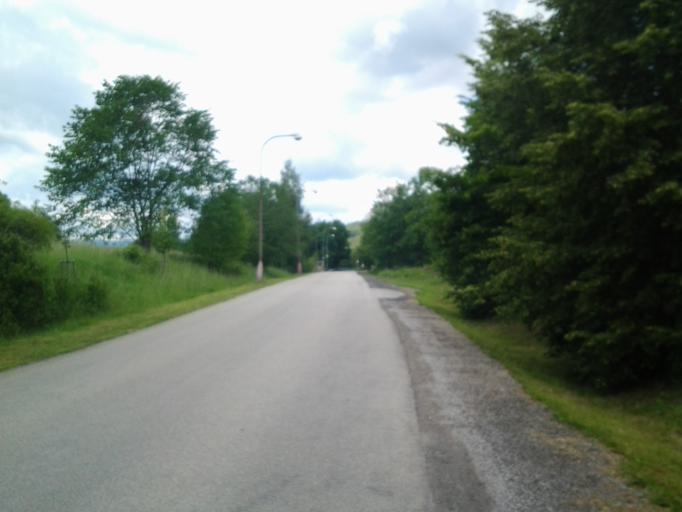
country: CZ
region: Jihocesky
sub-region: Okres Cesky Krumlov
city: Cesky Krumlov
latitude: 48.8279
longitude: 14.3060
